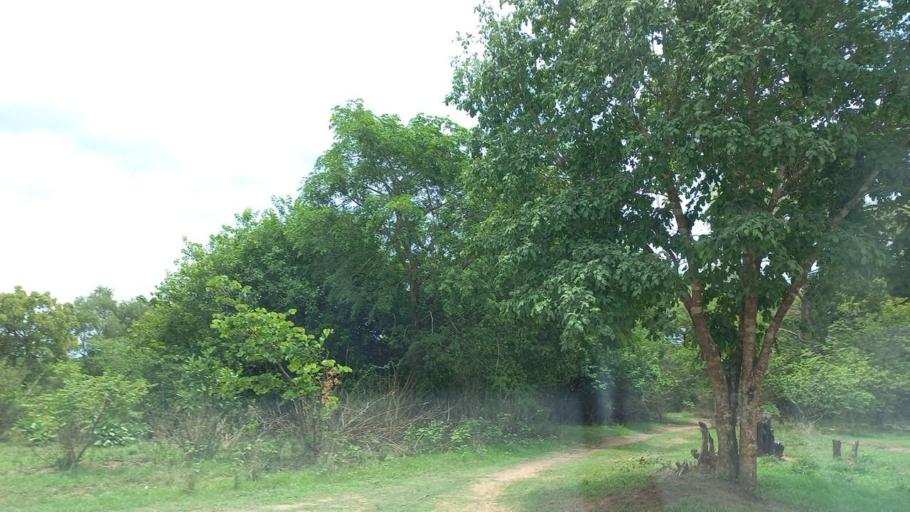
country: ZM
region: North-Western
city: Mufumbwe
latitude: -13.6948
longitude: 24.9779
